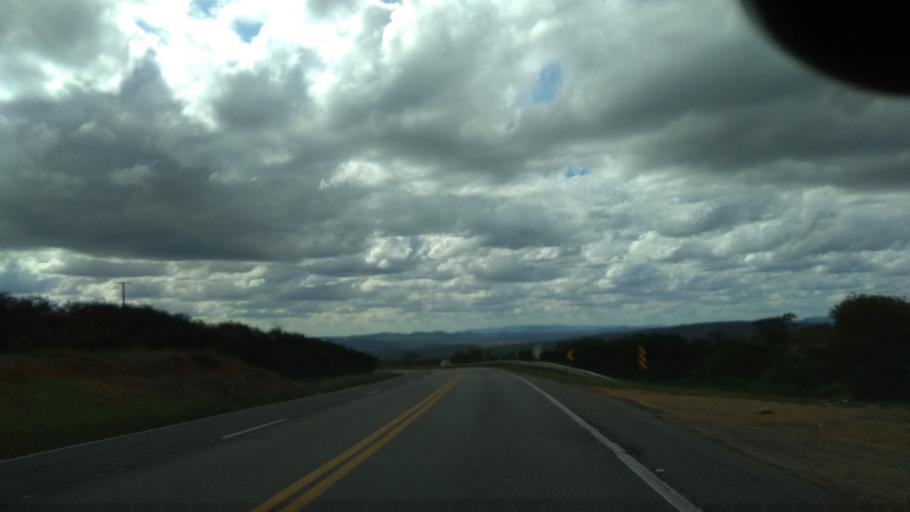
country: BR
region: Bahia
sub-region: Santa Ines
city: Santa Ines
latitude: -13.0615
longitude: -39.9570
